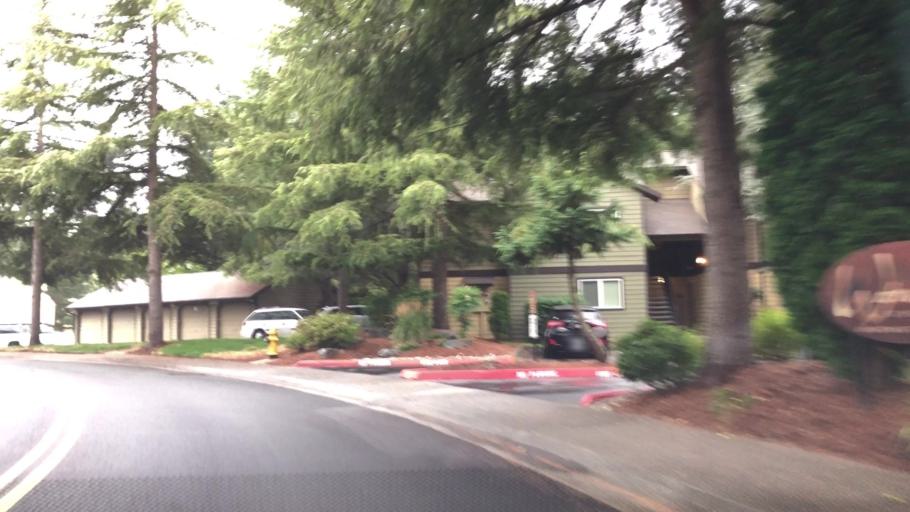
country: US
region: Washington
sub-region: Snohomish County
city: Mill Creek
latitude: 47.8296
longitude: -122.2052
